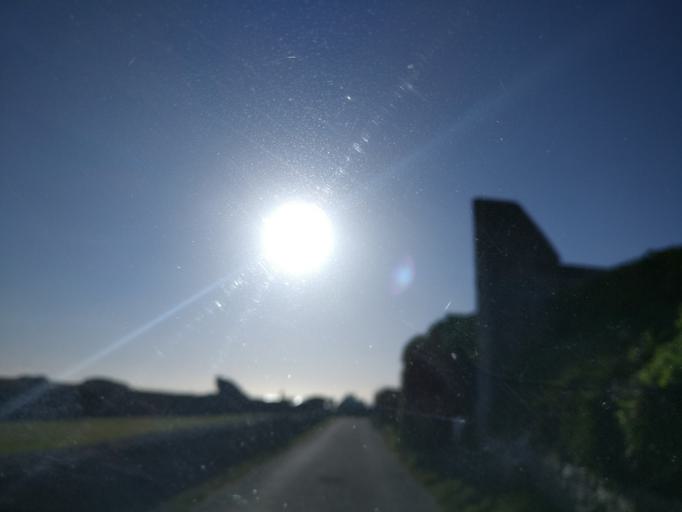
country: FR
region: Brittany
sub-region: Departement du Finistere
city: Porspoder
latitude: 48.5212
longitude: -4.7657
